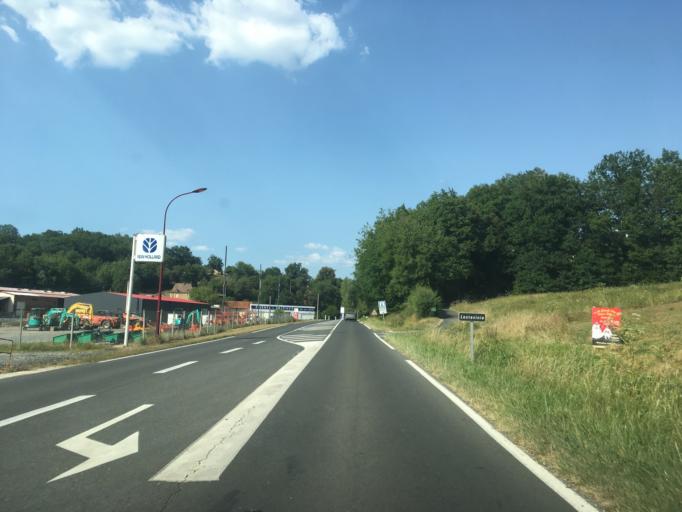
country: FR
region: Aquitaine
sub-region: Departement de la Dordogne
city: Cenac-et-Saint-Julien
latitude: 44.8479
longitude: 1.1798
